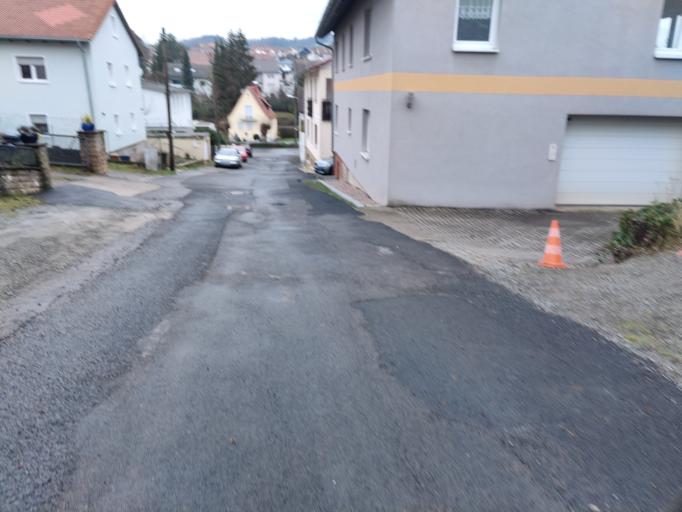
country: DE
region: Bavaria
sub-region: Regierungsbezirk Unterfranken
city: Bad Kissingen
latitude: 50.2030
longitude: 10.0966
